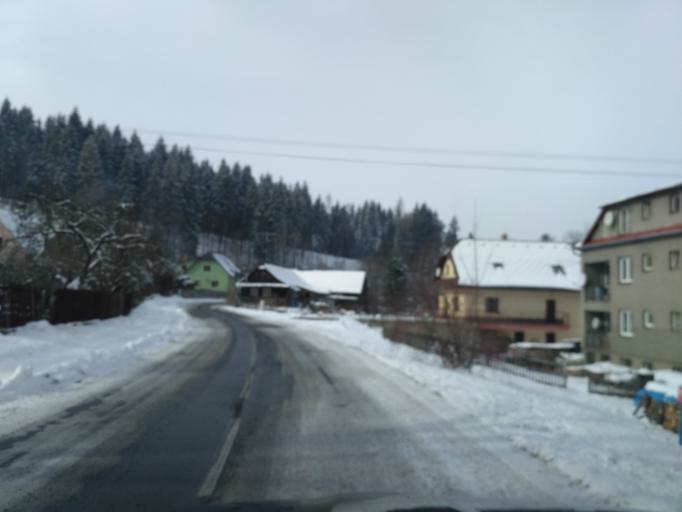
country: CZ
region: Zlin
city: Valasska Bystrice
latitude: 49.4197
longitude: 18.0887
